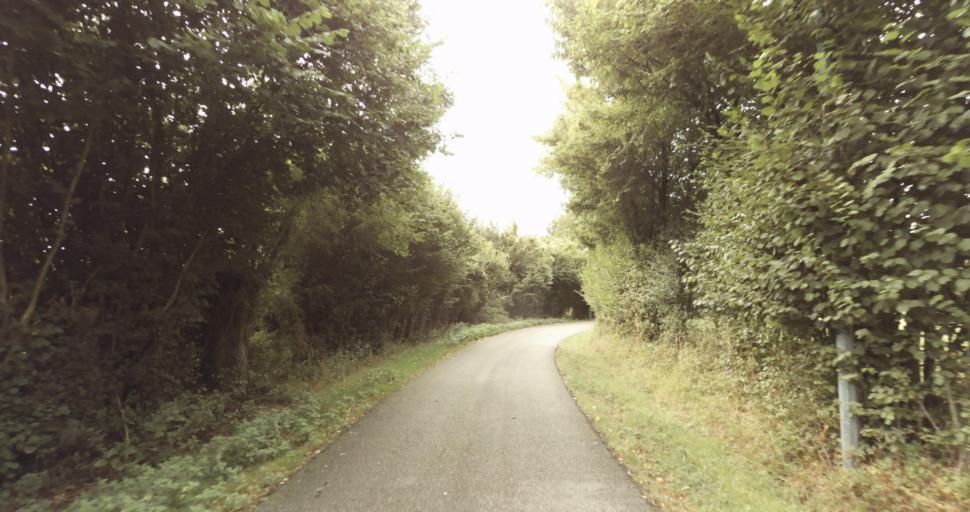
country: FR
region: Lower Normandy
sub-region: Departement de l'Orne
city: Gace
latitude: 48.7795
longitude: 0.3671
